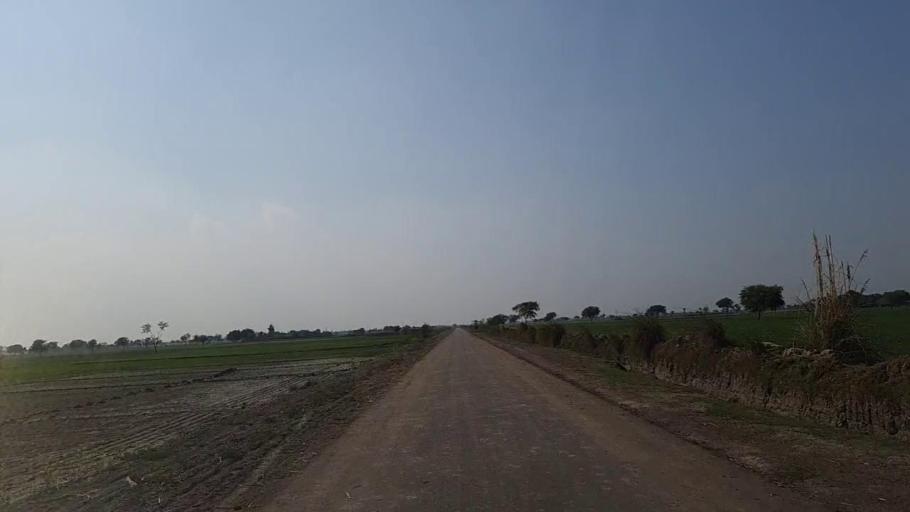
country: PK
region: Sindh
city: Jam Sahib
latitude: 26.3001
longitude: 68.5819
